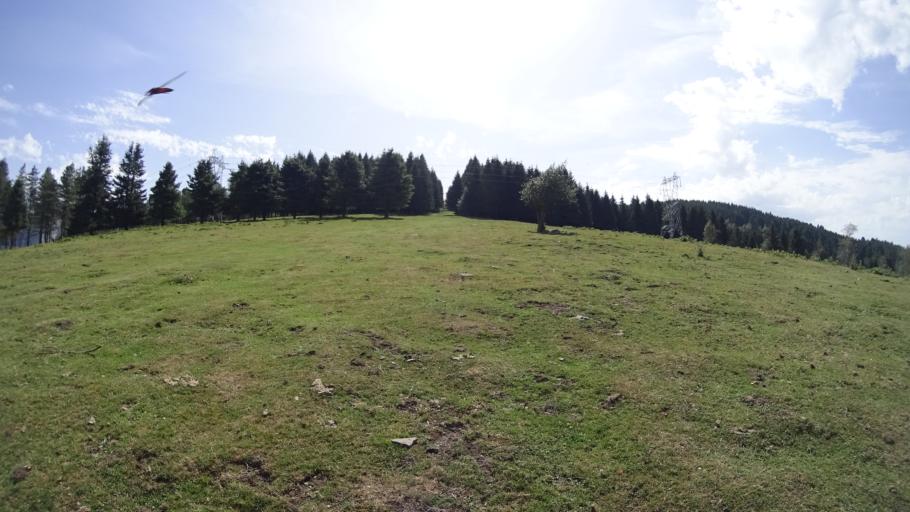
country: ES
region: Basque Country
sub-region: Bizkaia
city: Manaria
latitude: 43.0986
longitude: -2.6385
